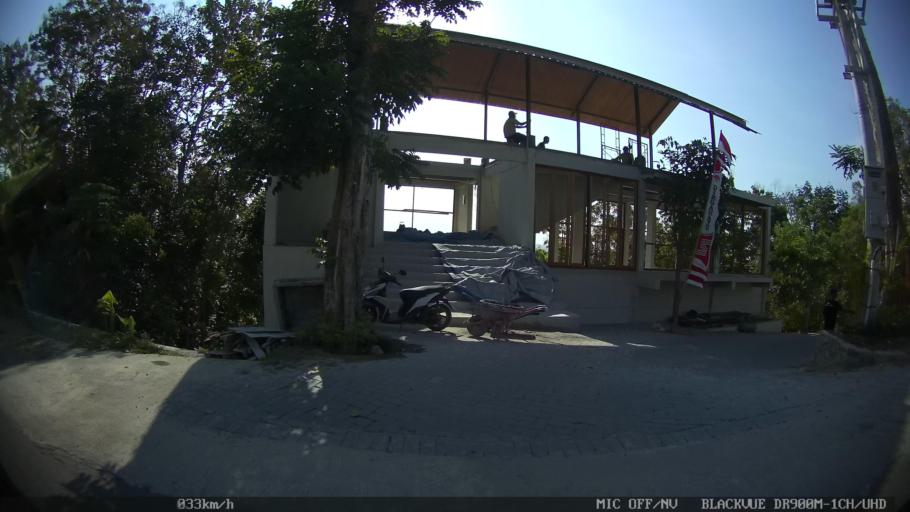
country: ID
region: Daerah Istimewa Yogyakarta
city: Kasihan
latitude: -7.8315
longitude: 110.2877
